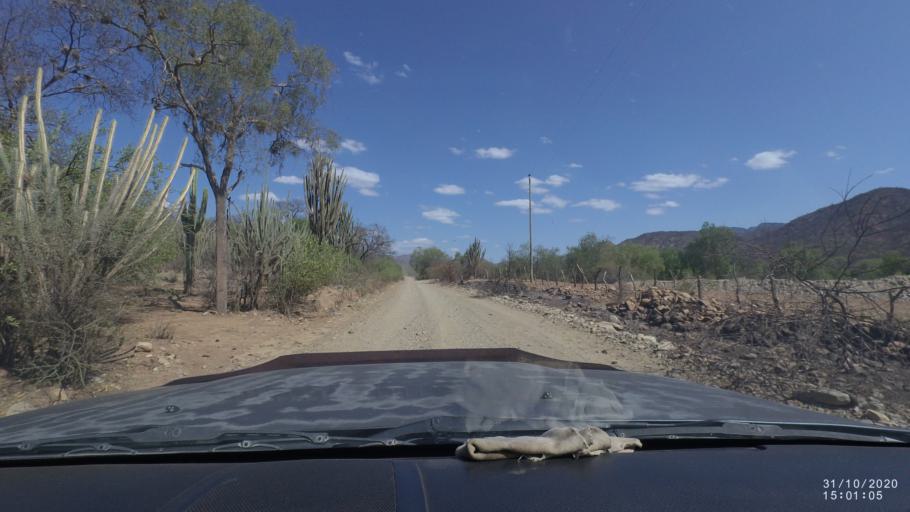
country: BO
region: Cochabamba
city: Aiquile
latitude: -18.2612
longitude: -64.8215
